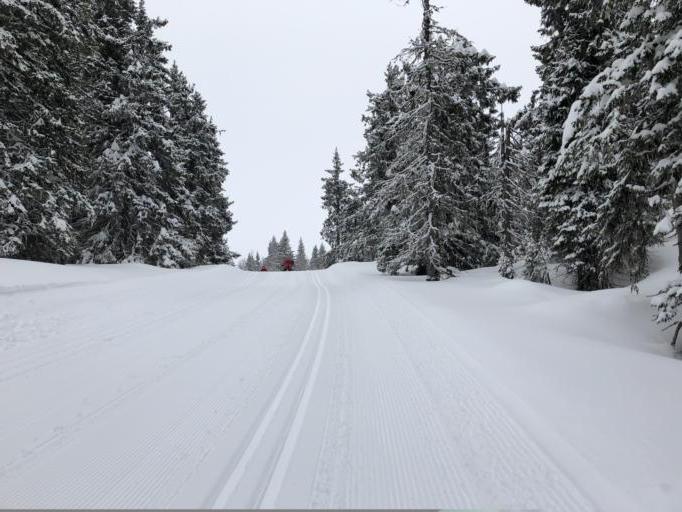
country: NO
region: Oppland
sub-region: Gausdal
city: Segalstad bru
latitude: 61.3206
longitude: 10.0576
